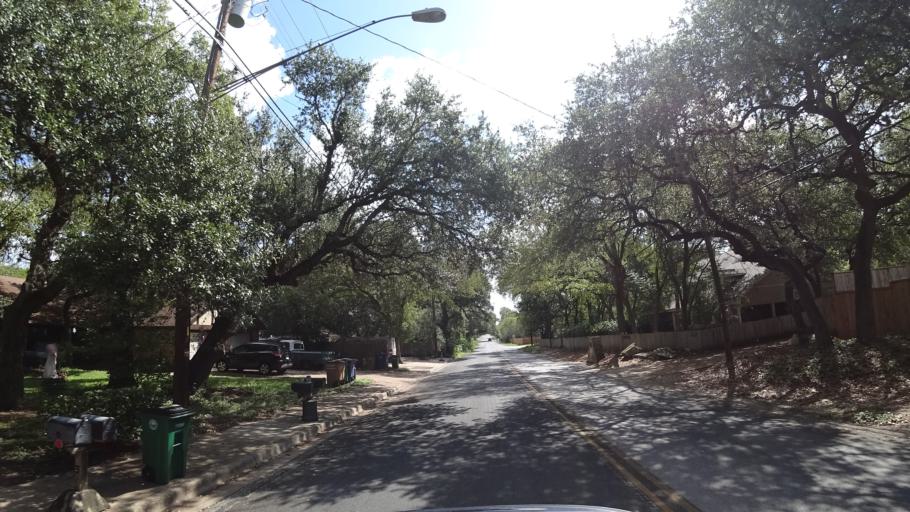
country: US
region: Texas
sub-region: Travis County
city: Onion Creek
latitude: 30.1970
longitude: -97.8009
